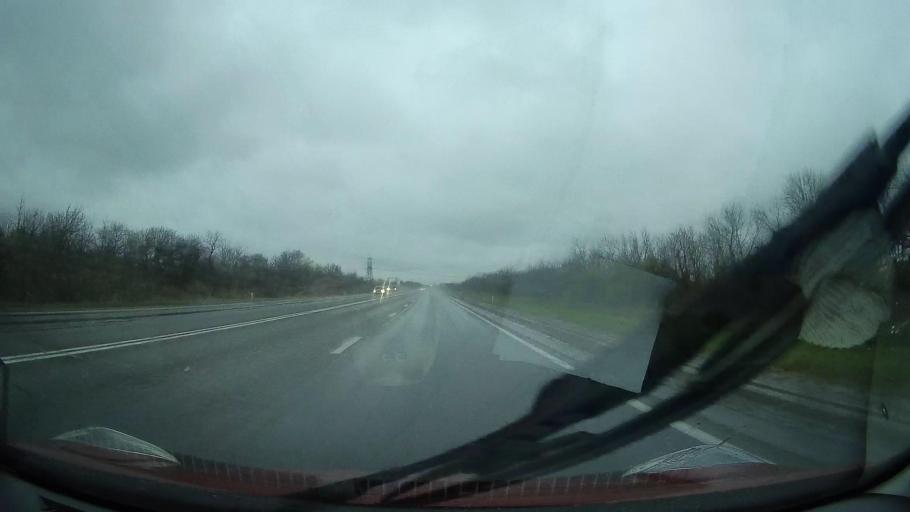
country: RU
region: Stavropol'skiy
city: Nevinnomyssk
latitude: 44.6332
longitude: 42.0129
